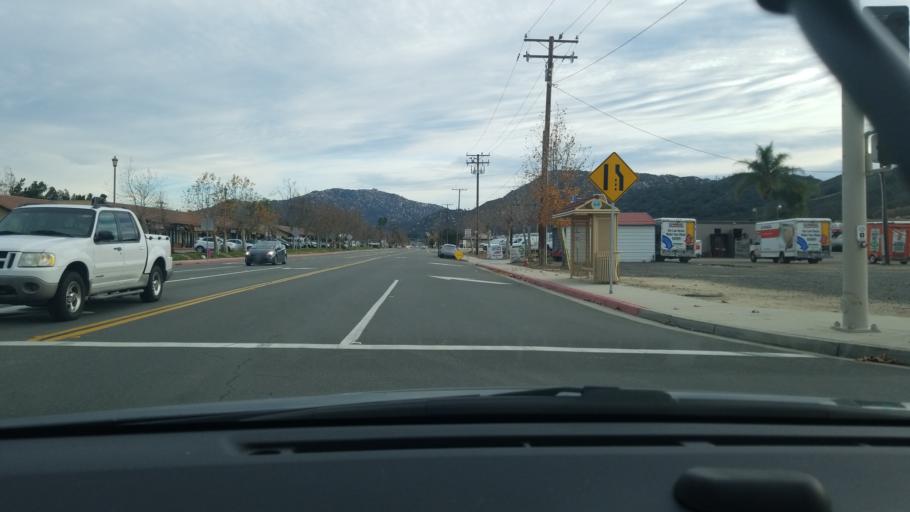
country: US
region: California
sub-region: Riverside County
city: Temecula
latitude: 33.4908
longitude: -117.1460
